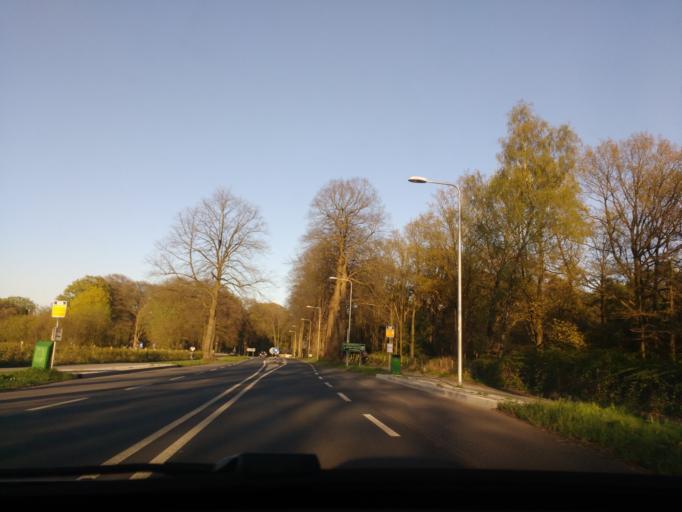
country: NL
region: Utrecht
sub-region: Gemeente Rhenen
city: Rhenen
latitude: 51.9548
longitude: 5.5974
